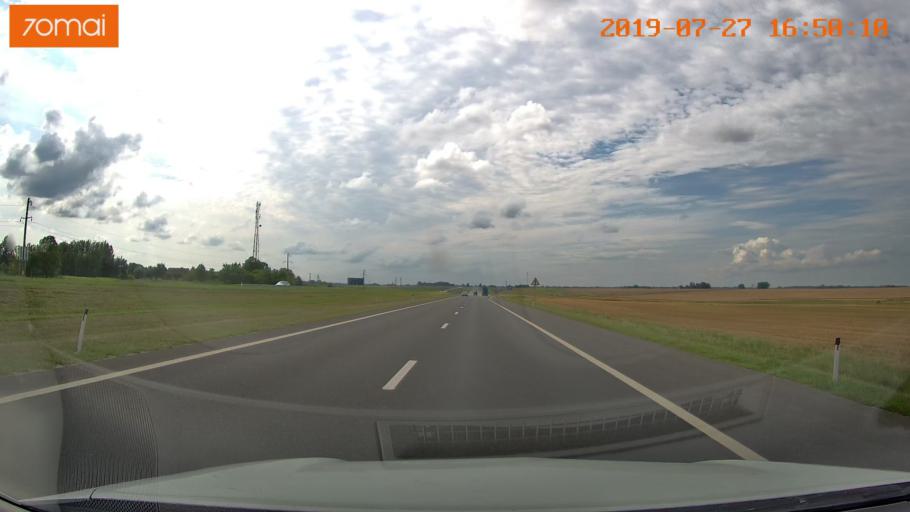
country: RU
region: Kaliningrad
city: Gvardeysk
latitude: 54.6762
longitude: 20.9210
